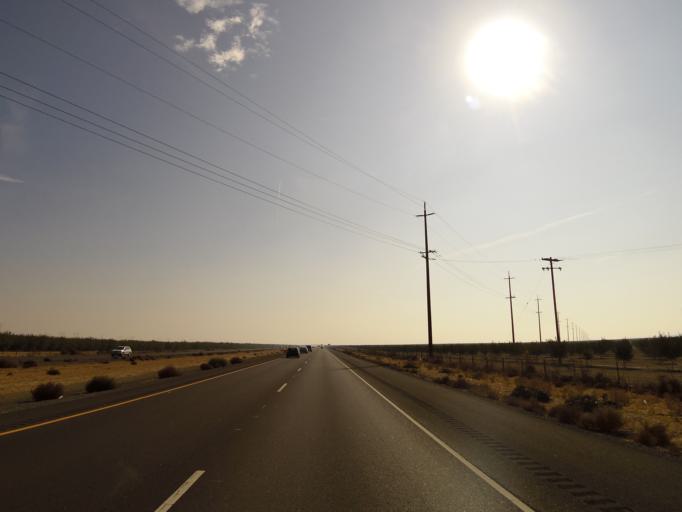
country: US
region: California
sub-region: Kings County
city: Kettleman City
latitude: 35.9468
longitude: -119.9249
